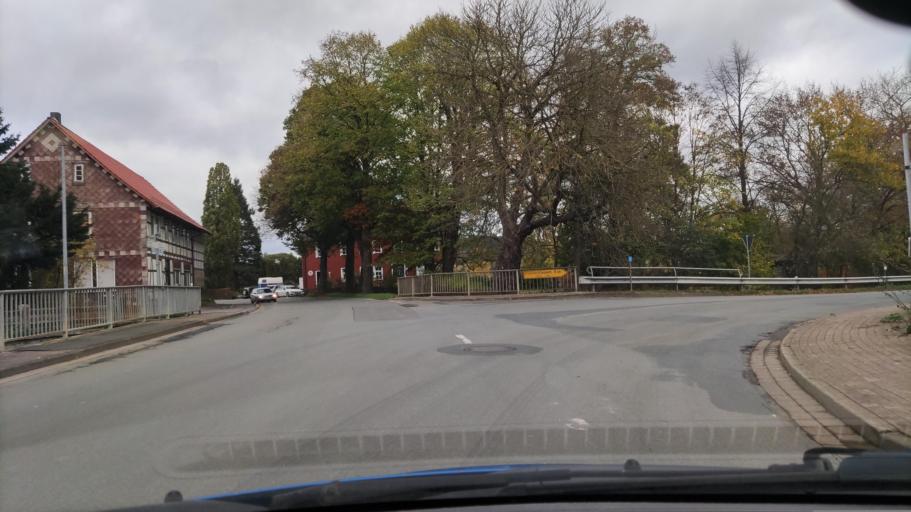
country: DE
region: Lower Saxony
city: Wangelnstedt
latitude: 51.8714
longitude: 9.6865
